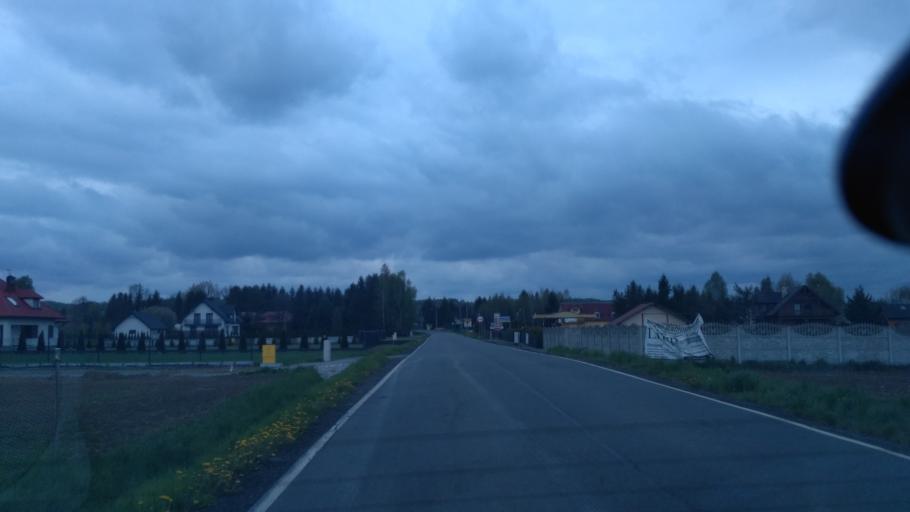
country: PL
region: Subcarpathian Voivodeship
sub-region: Powiat brzozowski
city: Turze Pole
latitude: 49.6571
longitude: 21.9927
